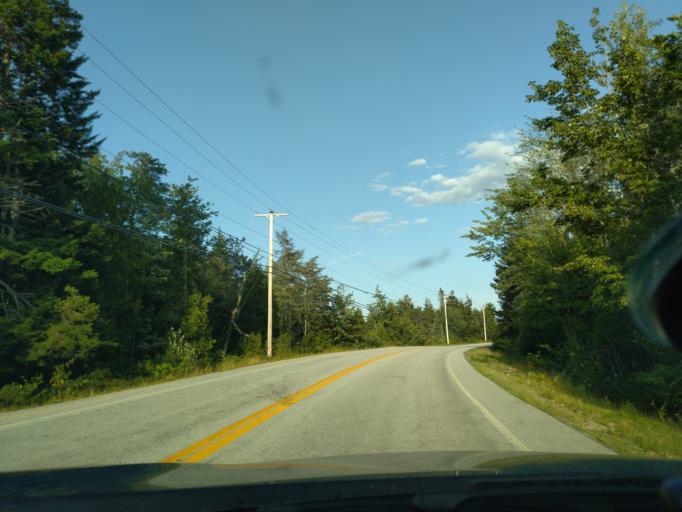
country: US
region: Maine
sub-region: Hancock County
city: Gouldsboro
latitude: 44.3940
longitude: -68.0658
